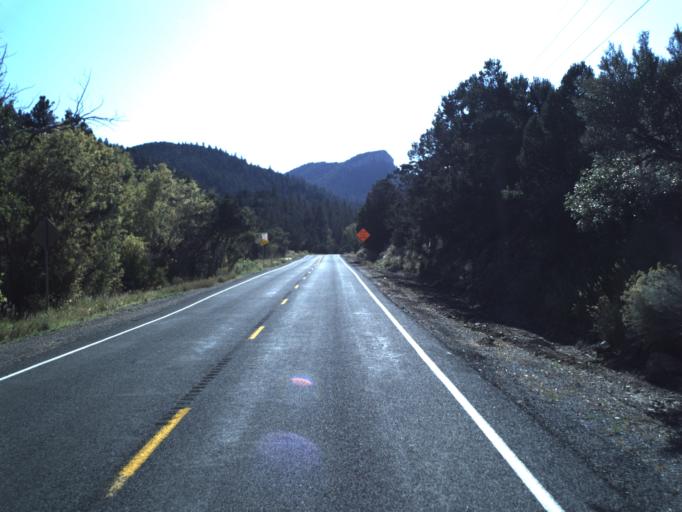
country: US
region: Utah
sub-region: Iron County
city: Parowan
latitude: 37.7710
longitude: -112.8421
